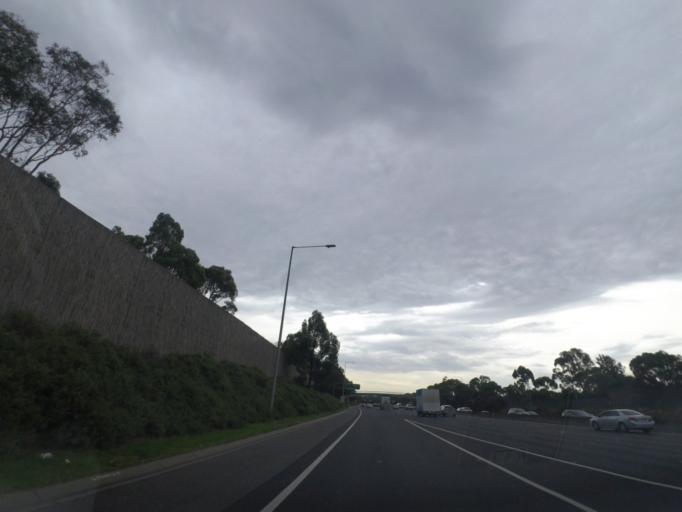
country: AU
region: Victoria
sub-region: Whitehorse
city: Box Hill North
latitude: -37.7982
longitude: 145.1382
